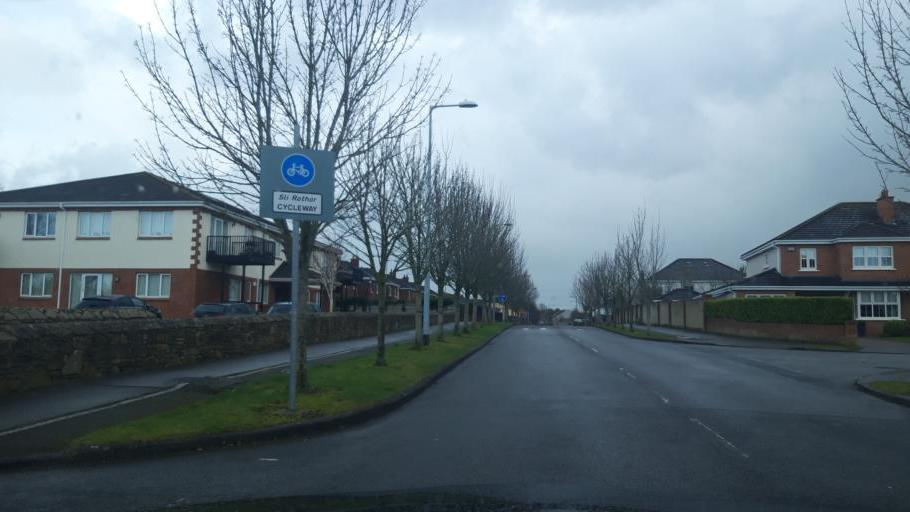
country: IE
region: Leinster
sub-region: Kildare
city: Celbridge
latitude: 53.3337
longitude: -6.5396
